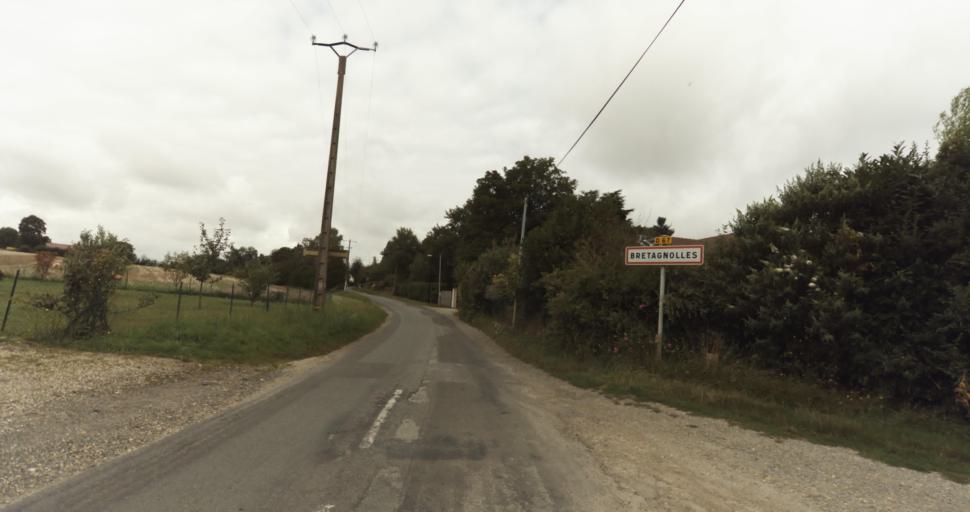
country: FR
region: Haute-Normandie
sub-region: Departement de l'Eure
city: Pacy-sur-Eure
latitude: 48.9506
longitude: 1.3555
